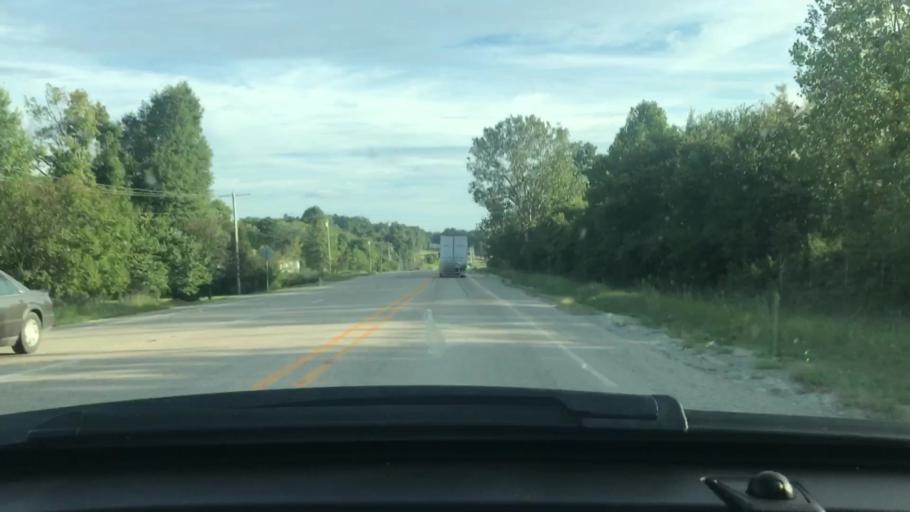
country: US
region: Arkansas
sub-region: Lawrence County
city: Hoxie
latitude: 36.1414
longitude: -91.1581
